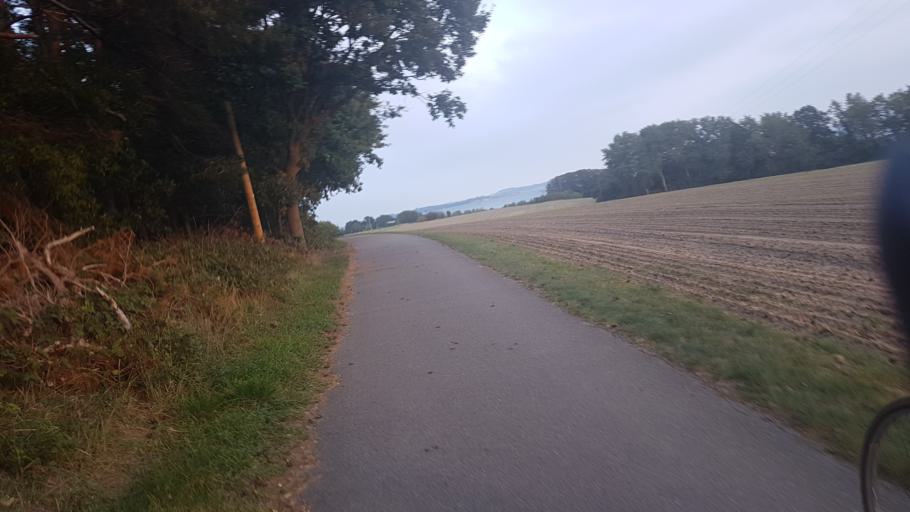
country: DE
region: Mecklenburg-Vorpommern
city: Putbus
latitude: 54.3440
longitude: 13.5431
